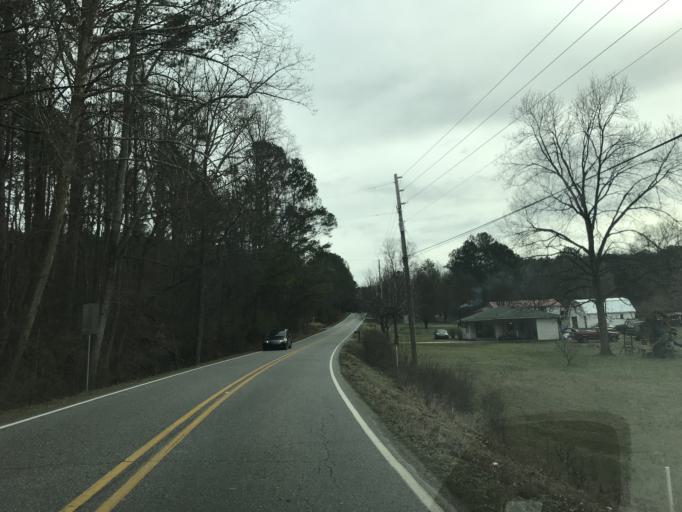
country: US
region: Georgia
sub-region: Cherokee County
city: Canton
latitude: 34.2022
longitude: -84.3879
